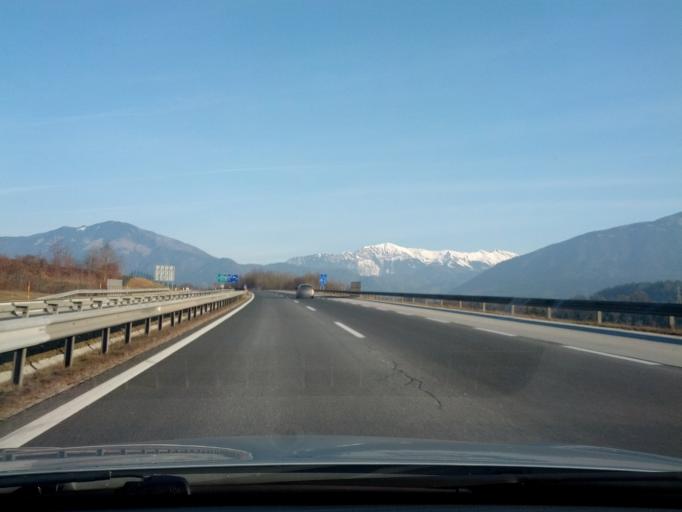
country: SI
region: Naklo
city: Naklo
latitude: 46.2990
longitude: 14.2839
